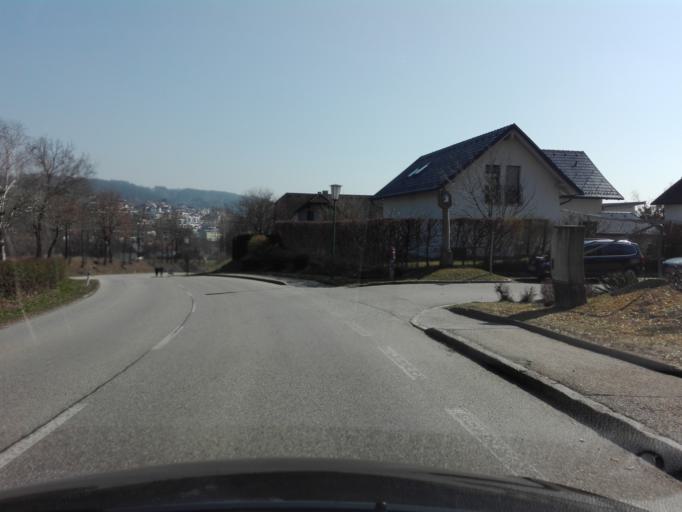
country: AT
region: Upper Austria
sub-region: Politischer Bezirk Urfahr-Umgebung
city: Engerwitzdorf
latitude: 48.3658
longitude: 14.4627
